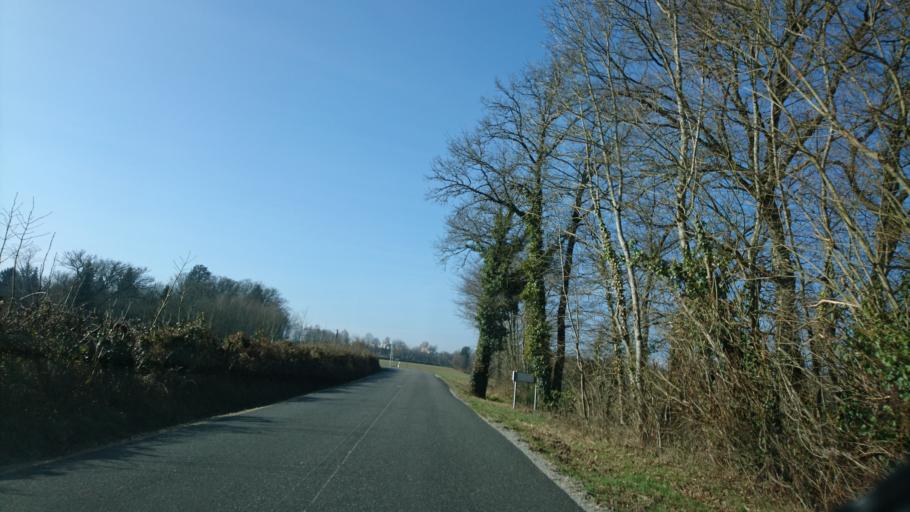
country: FR
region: Limousin
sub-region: Departement de la Haute-Vienne
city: Rilhac-Rancon
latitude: 45.8844
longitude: 1.3092
